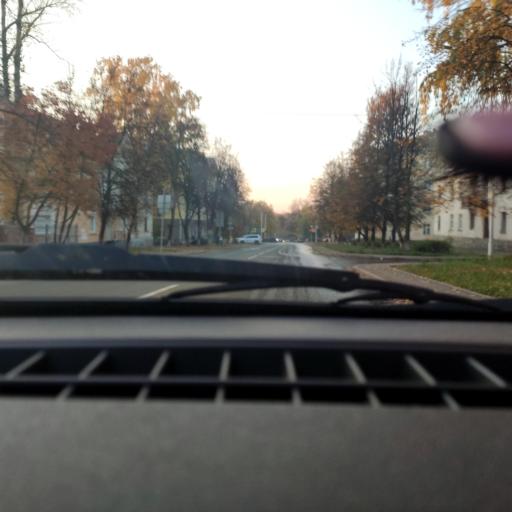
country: RU
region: Bashkortostan
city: Ufa
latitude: 54.8197
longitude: 56.0839
